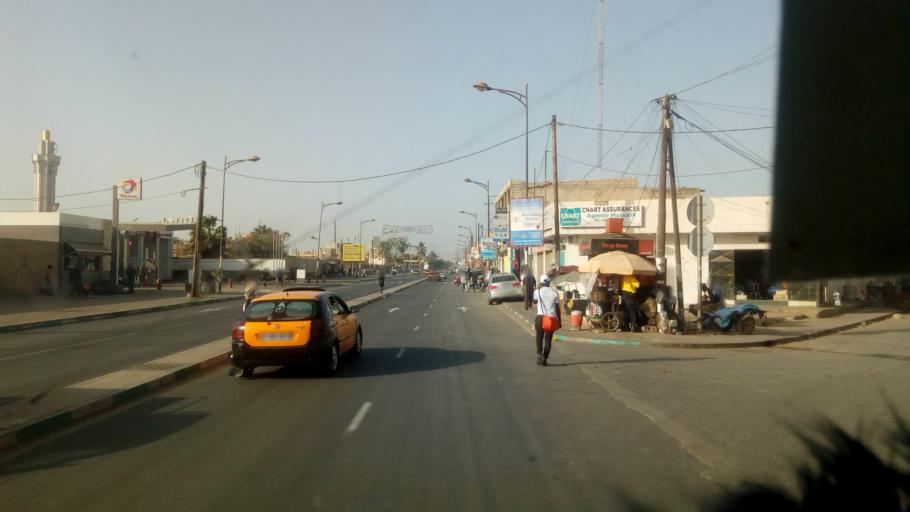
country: SN
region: Dakar
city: Dakar
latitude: 14.6992
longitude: -17.4472
